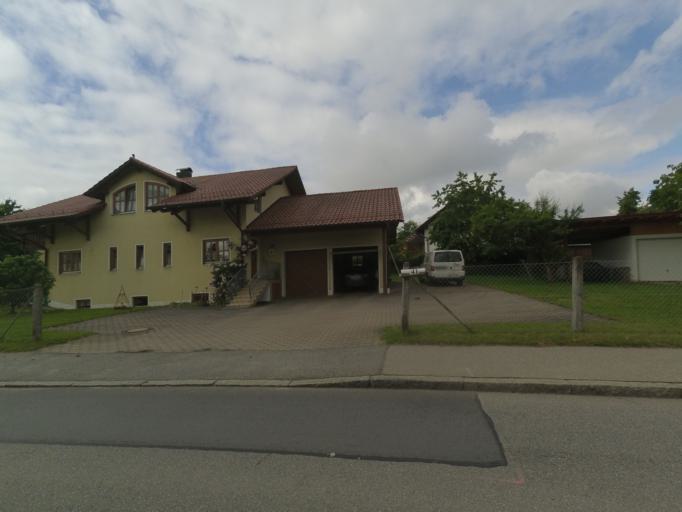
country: DE
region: Bavaria
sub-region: Lower Bavaria
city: Mitterfels
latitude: 48.9819
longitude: 12.6812
